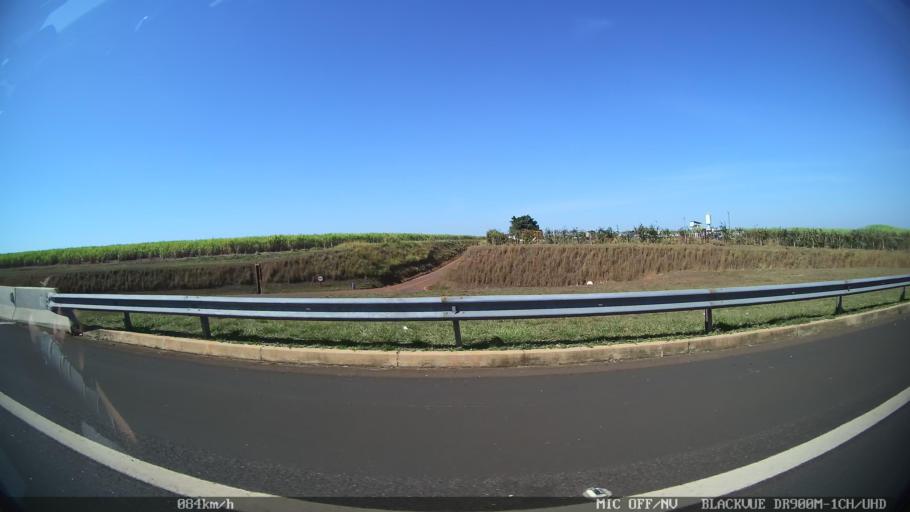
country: BR
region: Sao Paulo
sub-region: Batatais
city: Batatais
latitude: -20.8291
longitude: -47.5972
